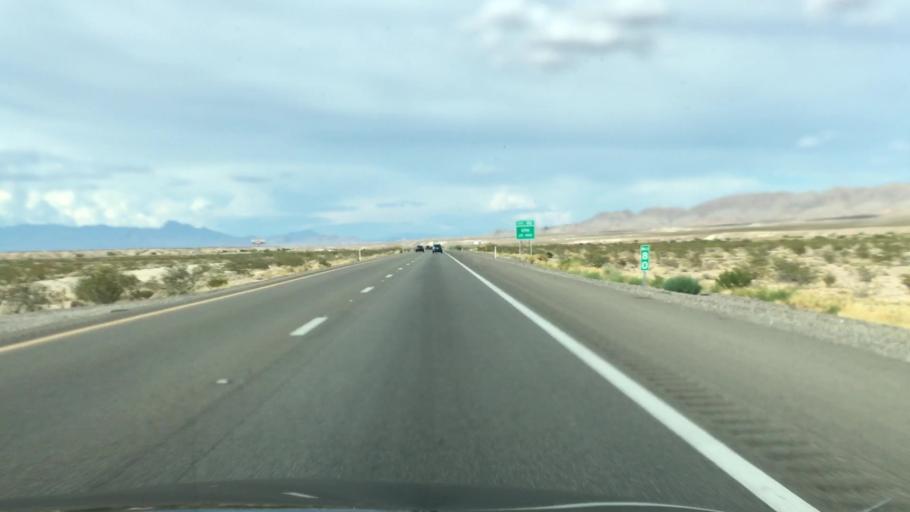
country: US
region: Nevada
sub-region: Clark County
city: Moapa Town
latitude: 36.5452
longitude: -114.7058
